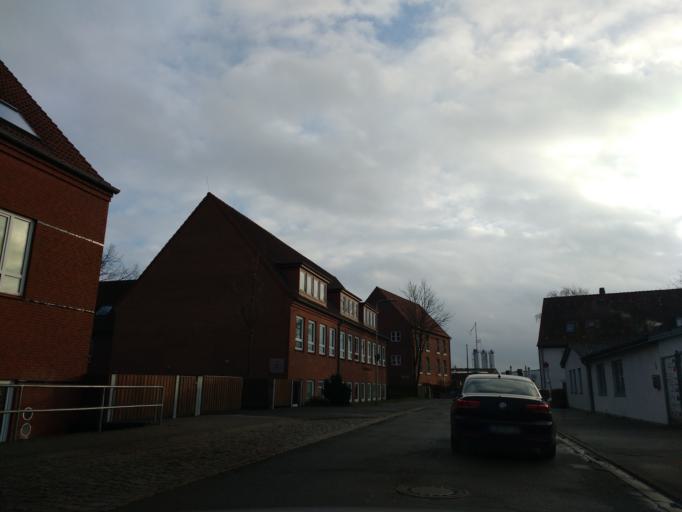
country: DE
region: Schleswig-Holstein
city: Eckernforde
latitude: 54.4735
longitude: 9.8281
